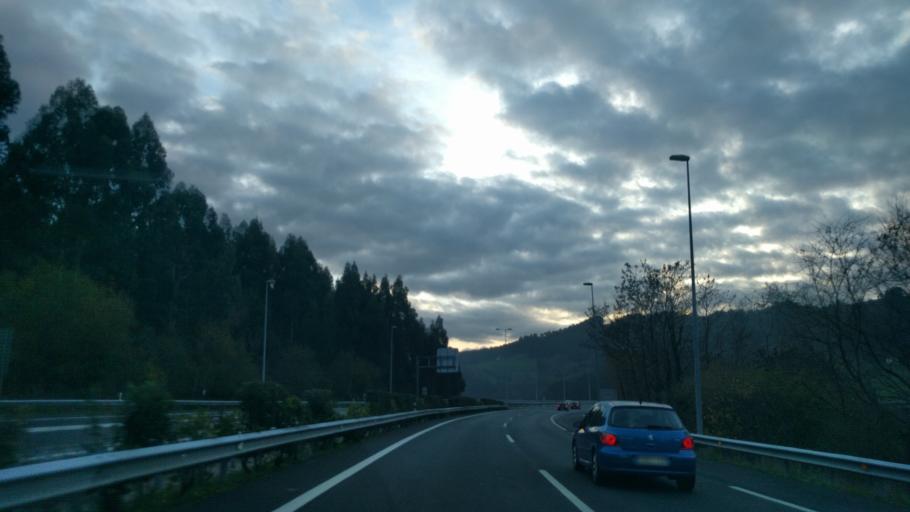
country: ES
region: Cantabria
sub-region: Provincia de Cantabria
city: Liendo
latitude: 43.3867
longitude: -3.3165
